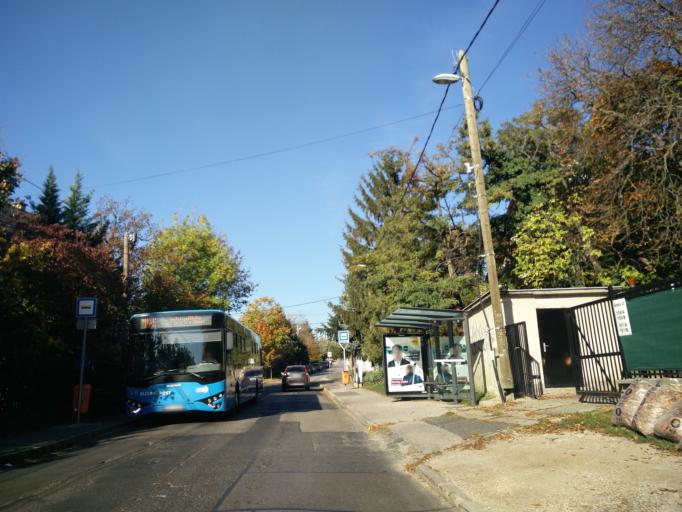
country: HU
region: Budapest
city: Budapest II. keruelet
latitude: 47.5232
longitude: 19.0027
